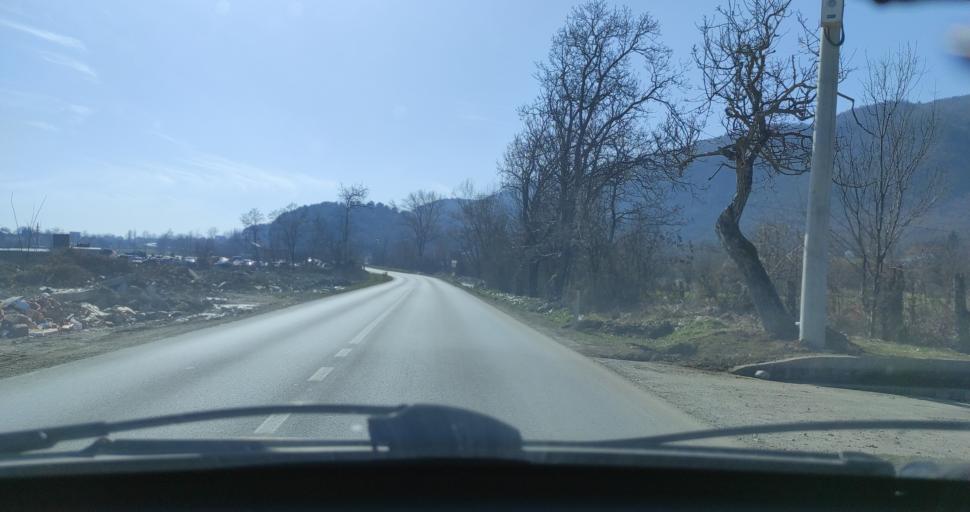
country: XK
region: Gjakova
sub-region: Komuna e Decanit
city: Strellc i Eperm
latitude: 42.5948
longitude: 20.2950
